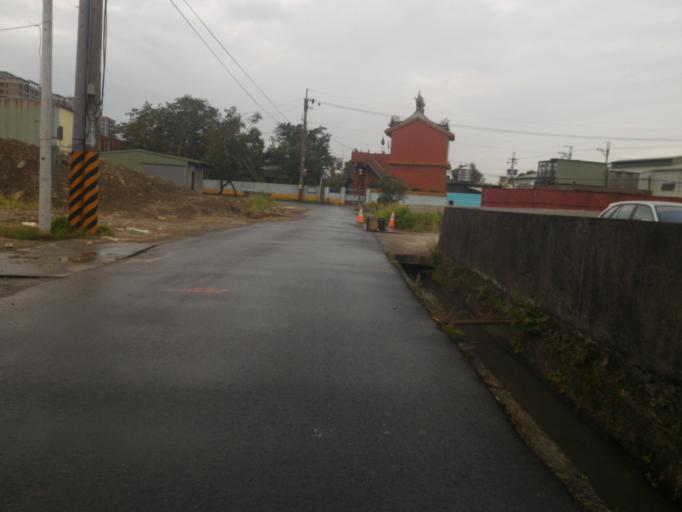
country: TW
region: Taiwan
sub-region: Taoyuan
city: Taoyuan
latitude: 24.9507
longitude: 121.3759
